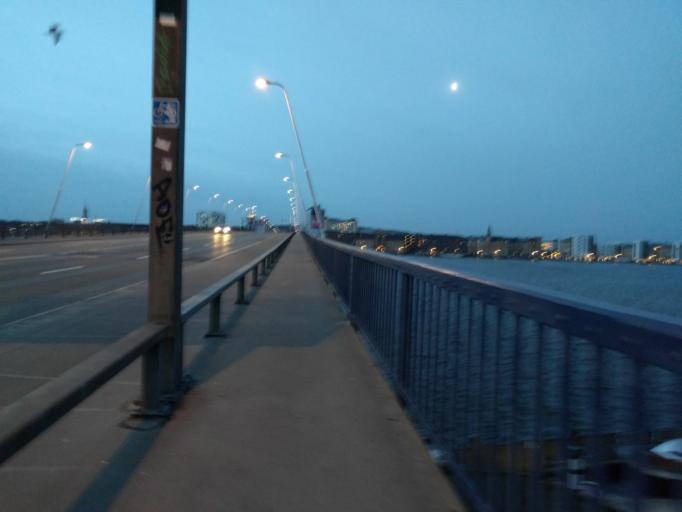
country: DK
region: North Denmark
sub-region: Alborg Kommune
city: Aalborg
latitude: 57.0563
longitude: 9.9214
